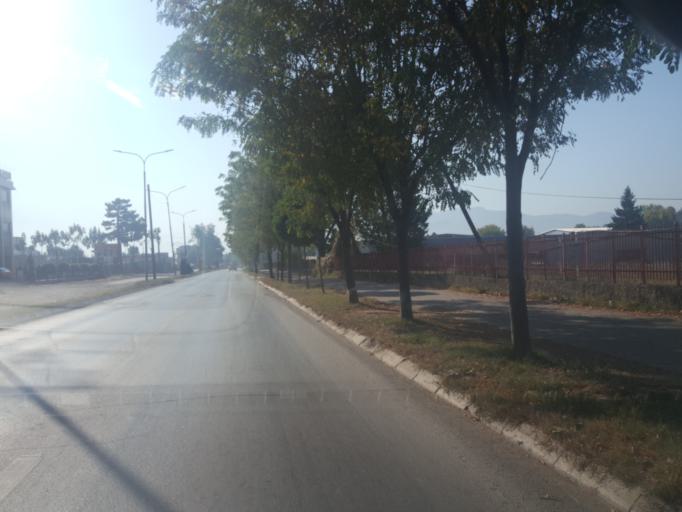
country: XK
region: Gjakova
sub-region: Komuna e Gjakoves
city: Gjakove
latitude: 42.3963
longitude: 20.4201
